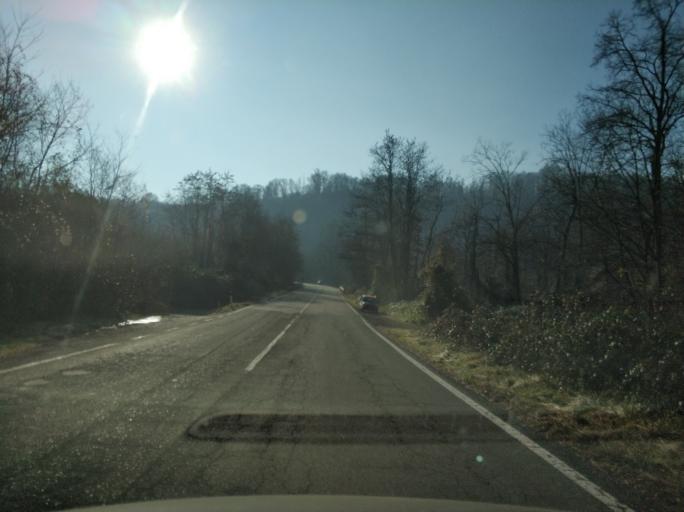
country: IT
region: Piedmont
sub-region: Provincia di Torino
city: Rocca Canavese
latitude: 45.2884
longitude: 7.5832
